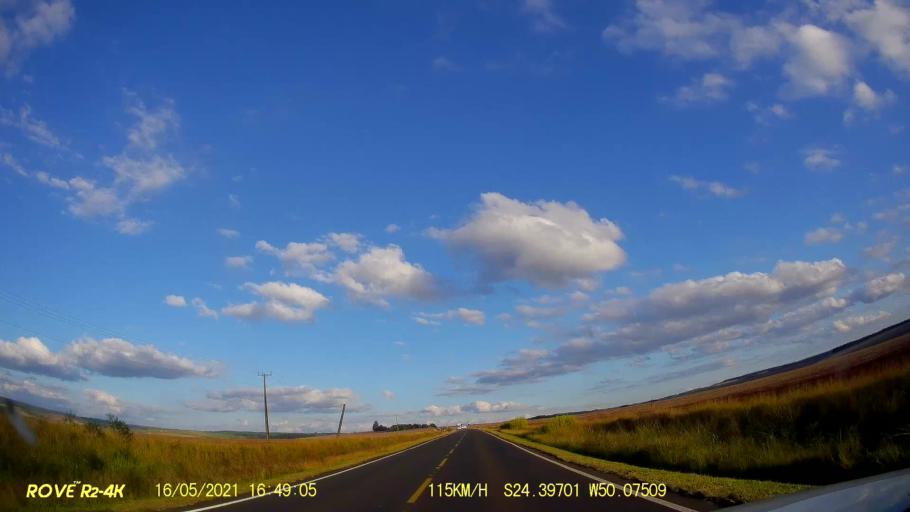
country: BR
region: Parana
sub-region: Pirai Do Sul
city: Pirai do Sul
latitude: -24.3973
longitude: -50.0748
